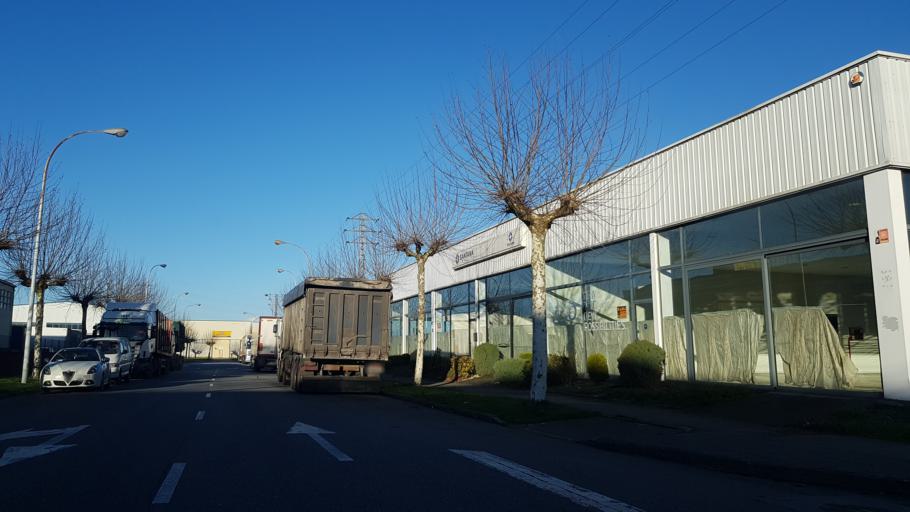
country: ES
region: Galicia
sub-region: Provincia de Lugo
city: Lugo
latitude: 43.0455
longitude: -7.5615
